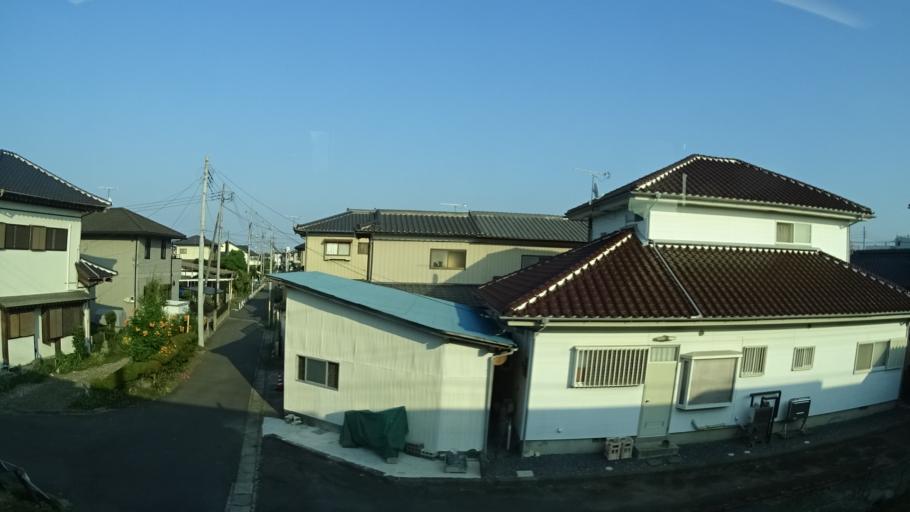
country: JP
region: Ibaraki
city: Funaishikawa
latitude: 36.4706
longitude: 140.5726
